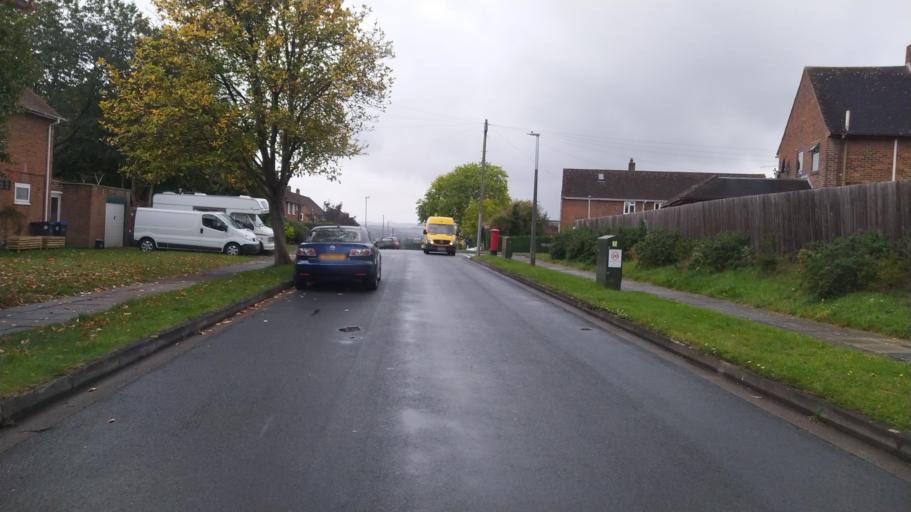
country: GB
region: England
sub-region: Wiltshire
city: Salisbury
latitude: 51.0870
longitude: -1.7937
